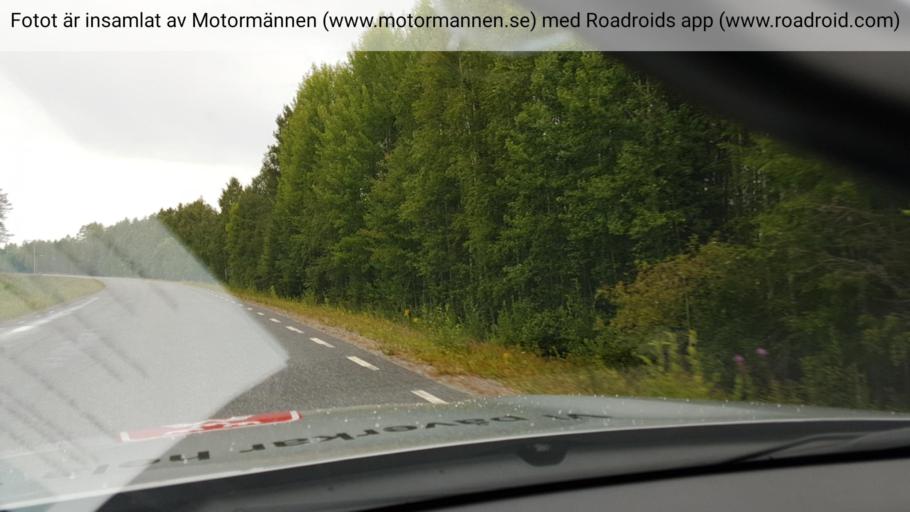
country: SE
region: Norrbotten
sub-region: Bodens Kommun
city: Boden
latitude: 65.8471
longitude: 21.4715
